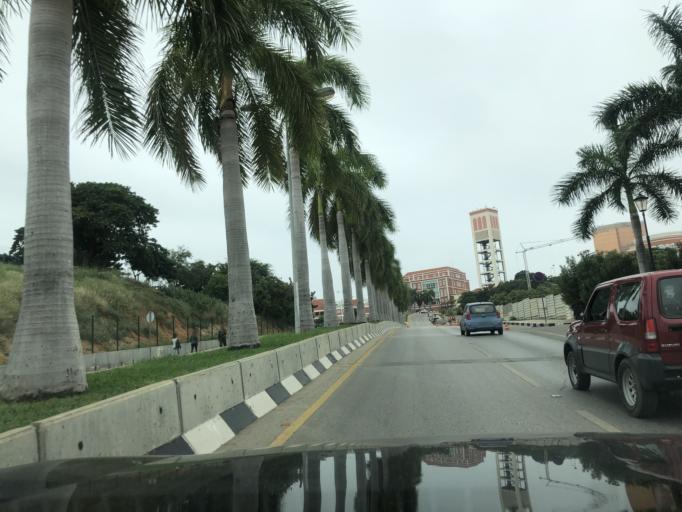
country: AO
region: Luanda
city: Luanda
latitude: -8.8211
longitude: 13.2236
